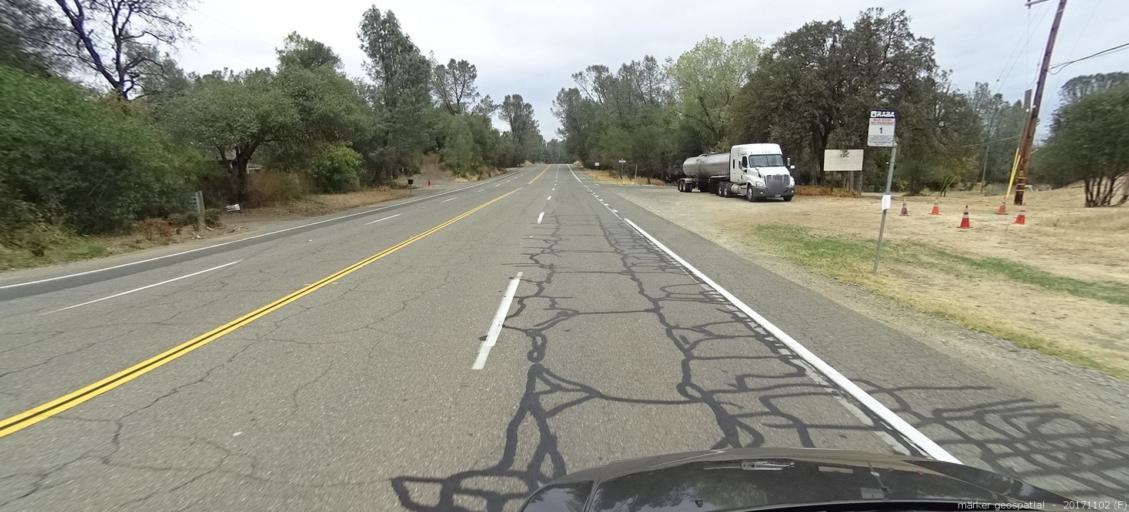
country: US
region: California
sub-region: Shasta County
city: Central Valley (historical)
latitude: 40.6564
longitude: -122.3966
